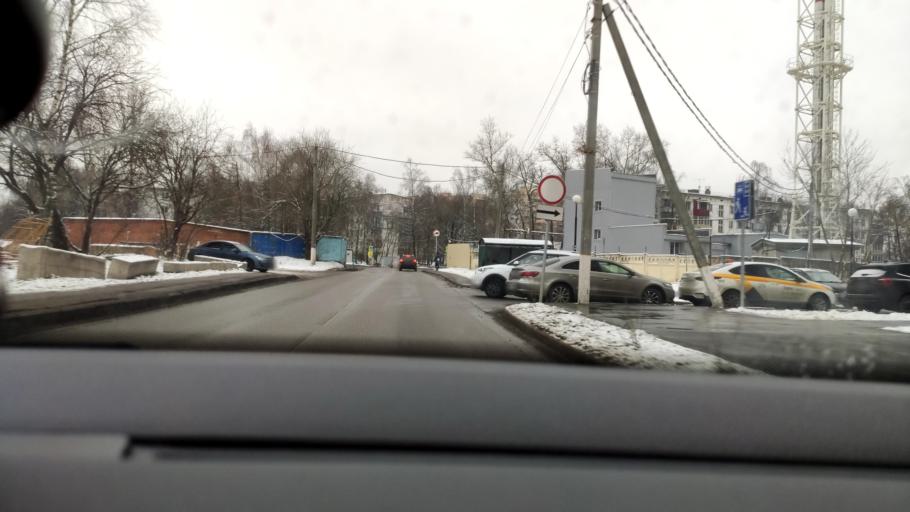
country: RU
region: Moskovskaya
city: Novopodrezkovo
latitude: 55.9547
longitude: 37.3298
